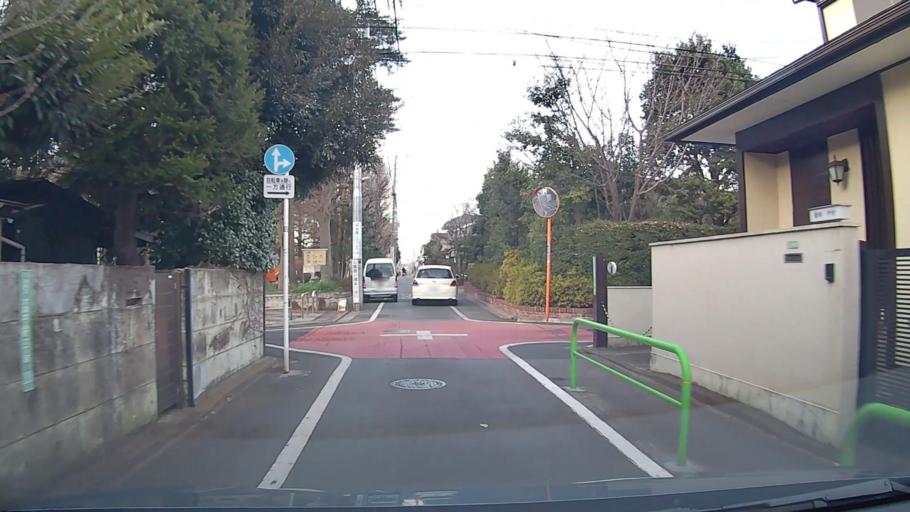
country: JP
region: Saitama
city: Asaka
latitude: 35.7713
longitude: 139.5837
